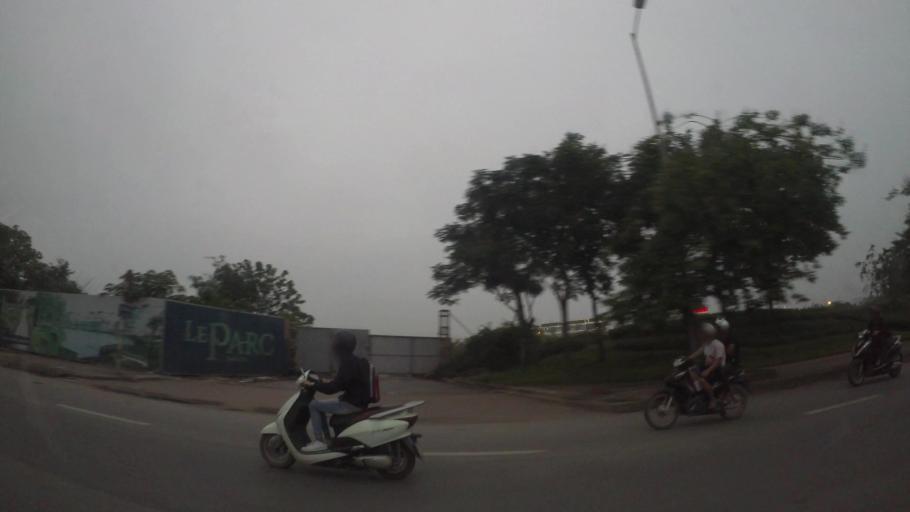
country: VN
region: Ha Noi
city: Van Dien
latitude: 20.9639
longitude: 105.8605
